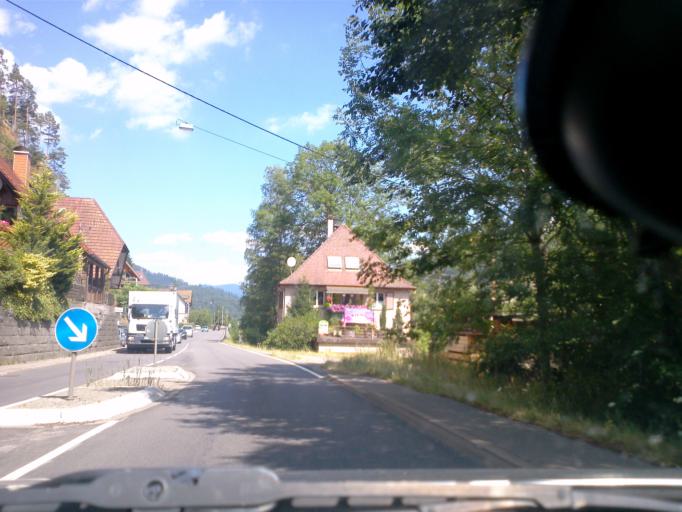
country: DE
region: Baden-Wuerttemberg
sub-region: Freiburg Region
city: Hornberg
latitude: 48.2249
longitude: 8.2225
